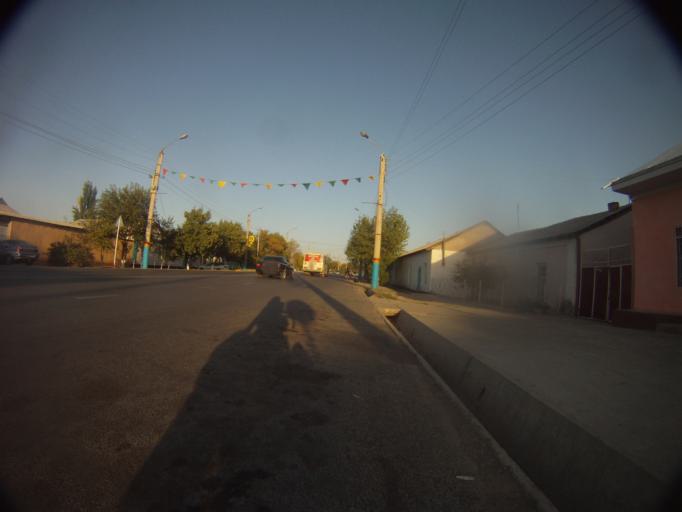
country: KZ
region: Ongtustik Qazaqstan
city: Turkestan
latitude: 43.2981
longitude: 68.2794
